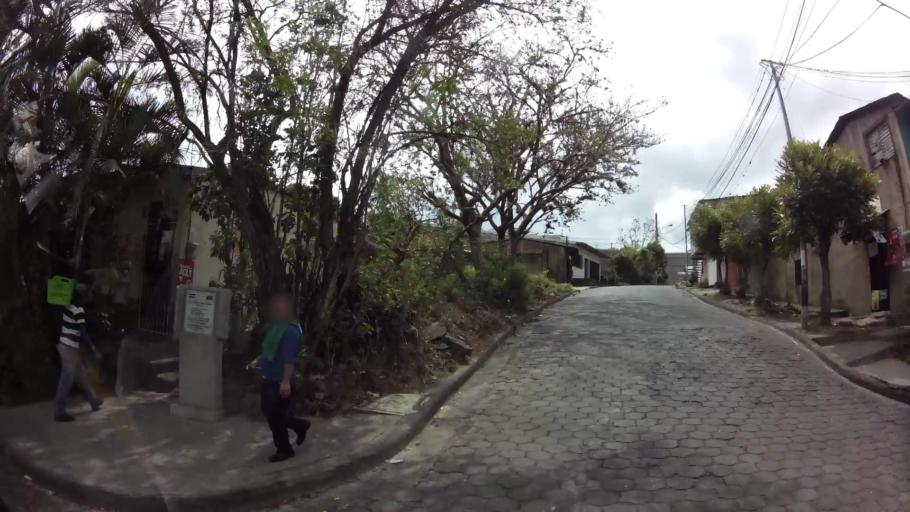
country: NI
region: Matagalpa
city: Matagalpa
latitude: 12.9196
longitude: -85.9178
